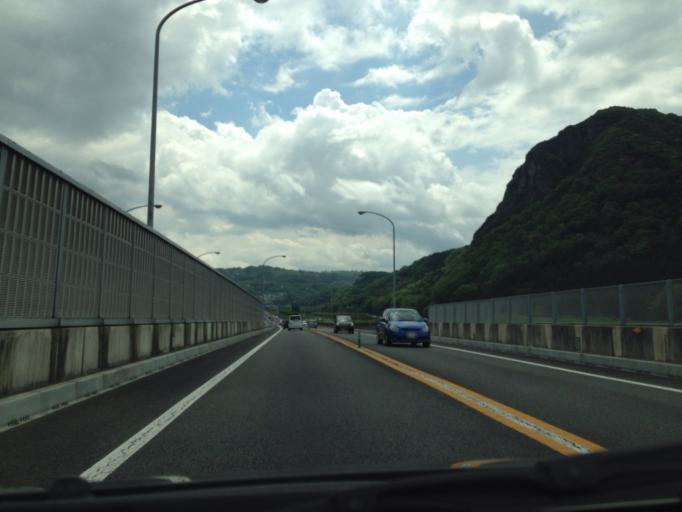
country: JP
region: Shizuoka
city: Mishima
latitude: 35.0099
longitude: 138.9399
